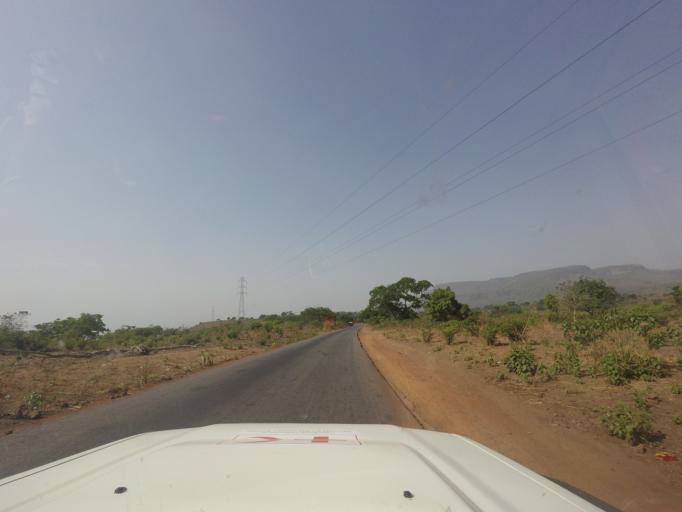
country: GN
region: Mamou
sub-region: Mamou Prefecture
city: Mamou
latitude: 10.2536
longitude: -12.4576
